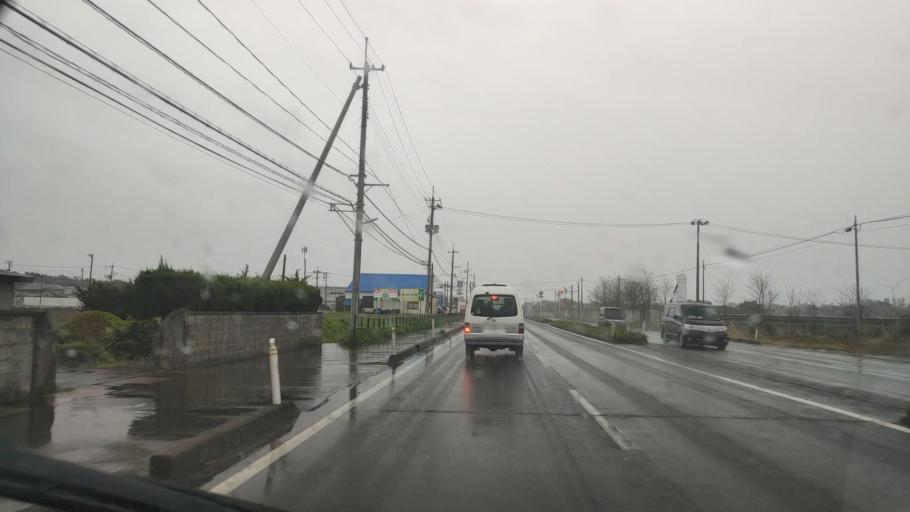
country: JP
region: Akita
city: Tenno
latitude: 39.8644
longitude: 140.0055
